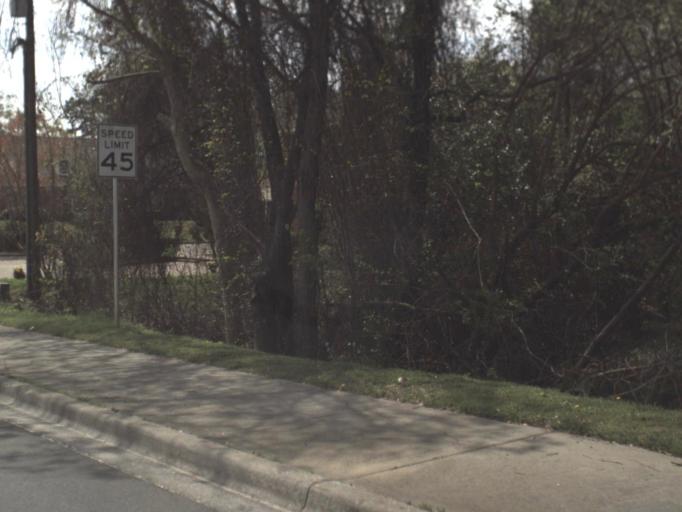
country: US
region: Florida
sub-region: Leon County
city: Tallahassee
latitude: 30.4992
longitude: -84.2473
